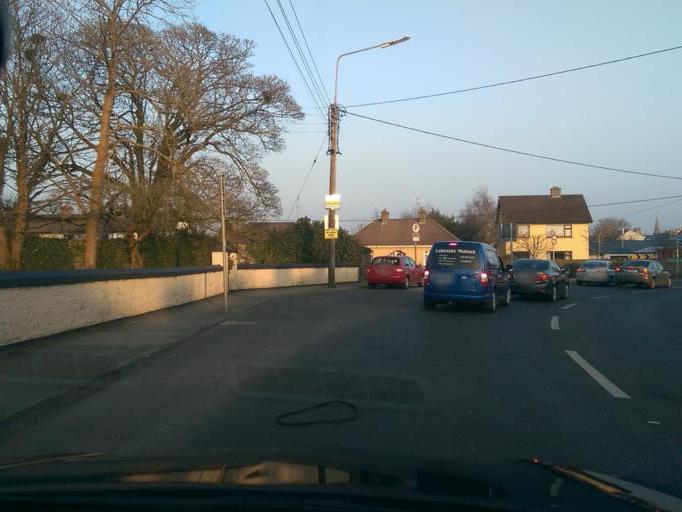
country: IE
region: Connaught
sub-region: County Galway
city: Loughrea
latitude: 53.2002
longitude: -8.5750
